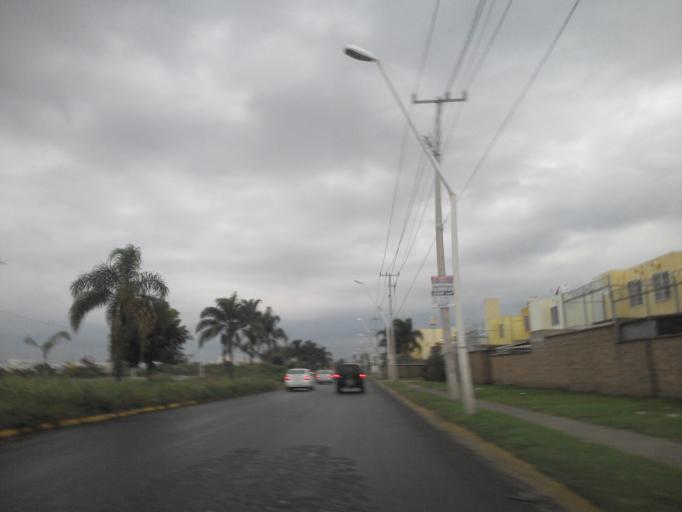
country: MX
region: Jalisco
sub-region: San Pedro Tlaquepaque
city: Paseo del Prado
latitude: 20.5791
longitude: -103.3879
